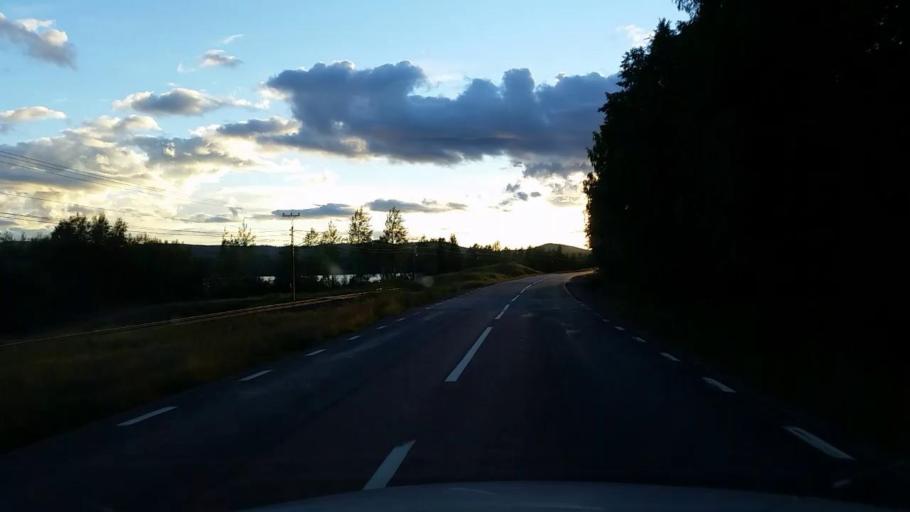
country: SE
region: Gaevleborg
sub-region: Ljusdals Kommun
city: Farila
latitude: 62.1305
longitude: 15.7014
